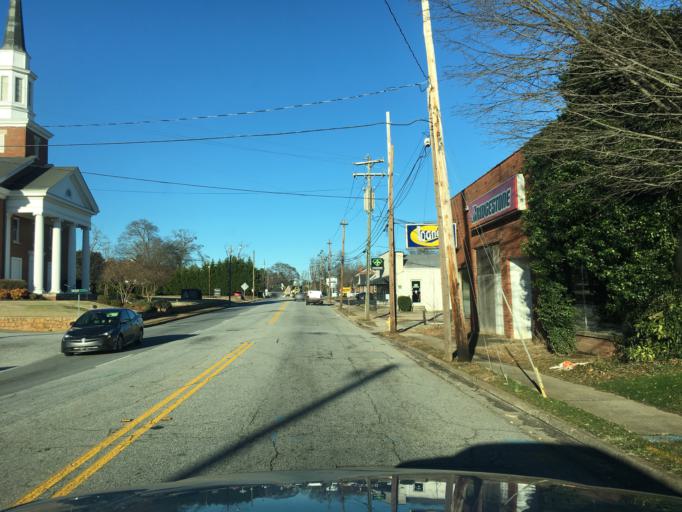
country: US
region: South Carolina
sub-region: Greenville County
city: Greer
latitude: 34.9400
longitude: -82.2260
